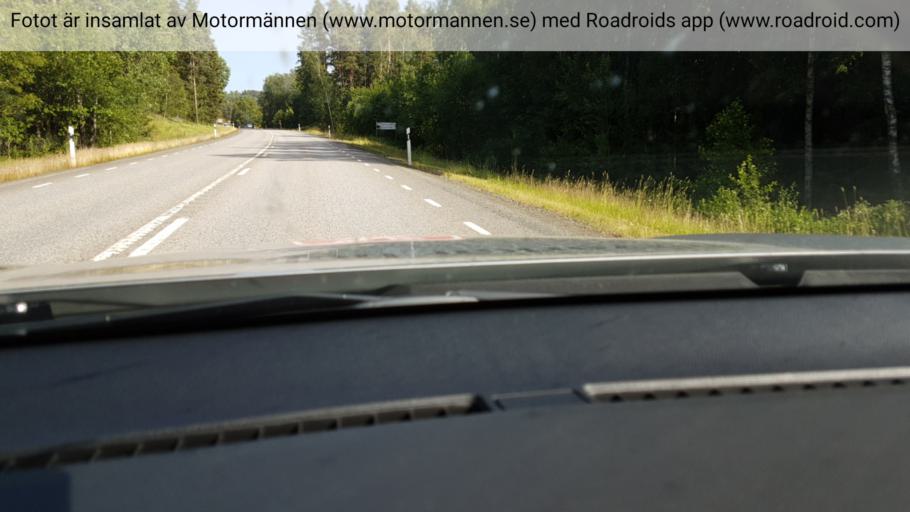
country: SE
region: Joenkoeping
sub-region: Eksjo Kommun
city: Eksjoe
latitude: 57.7610
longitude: 14.9129
